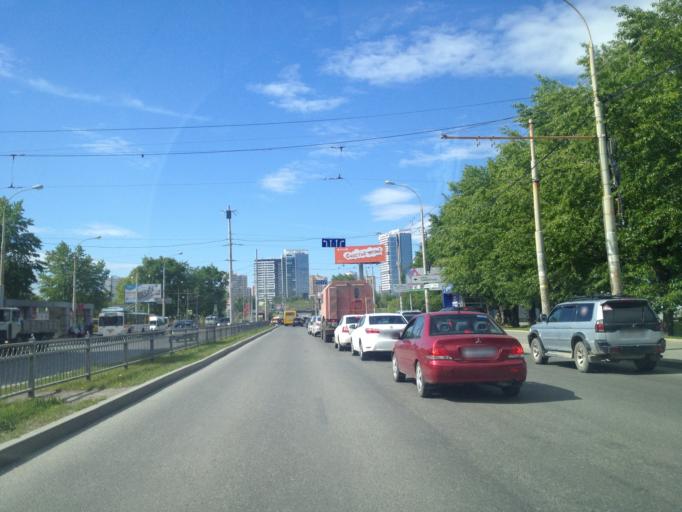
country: RU
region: Sverdlovsk
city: Yekaterinburg
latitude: 56.7912
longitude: 60.6444
